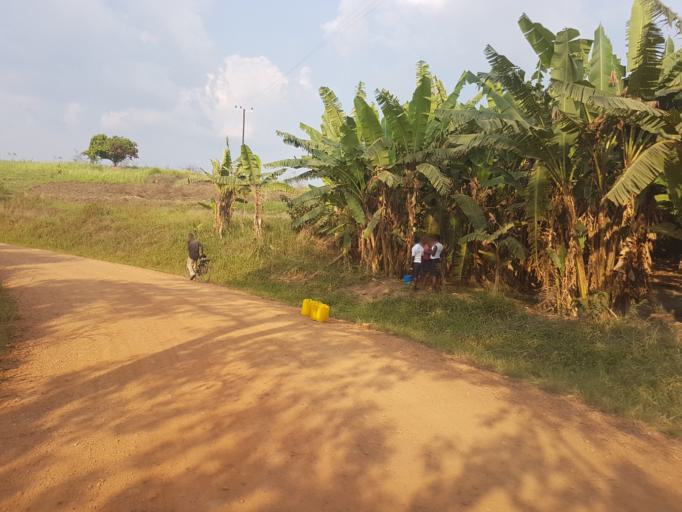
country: UG
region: Western Region
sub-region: Rukungiri District
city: Rukungiri
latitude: -0.6531
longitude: 29.8549
